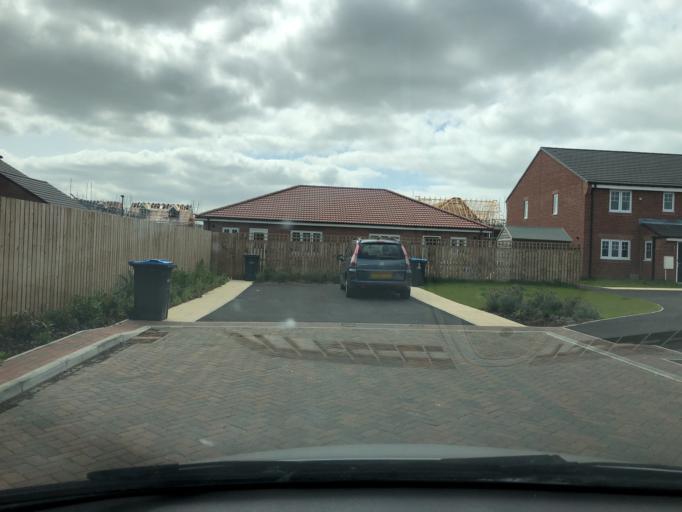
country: GB
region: England
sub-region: North Yorkshire
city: Thirsk
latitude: 54.2212
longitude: -1.3562
